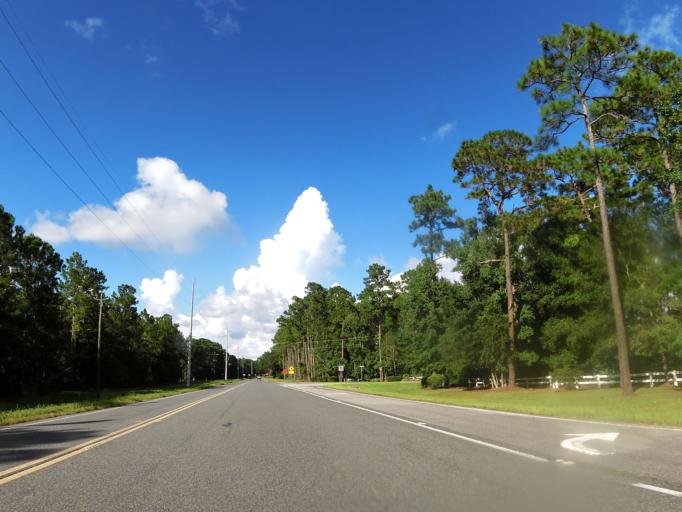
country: US
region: Georgia
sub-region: Glynn County
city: Dock Junction
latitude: 31.1306
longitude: -81.6006
